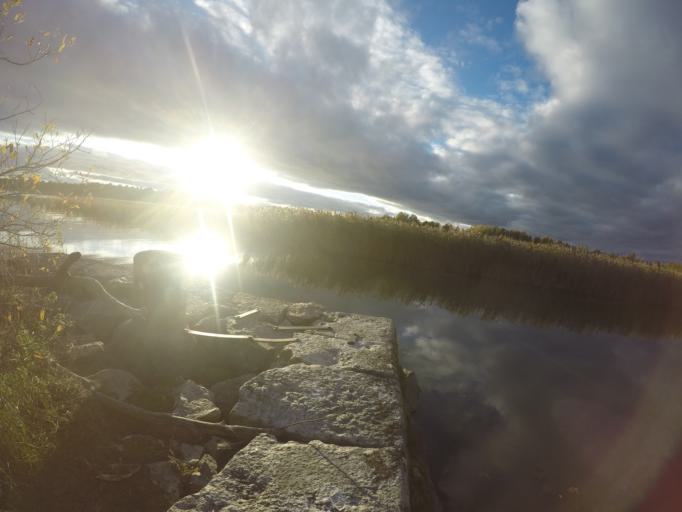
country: SE
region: Vaestmanland
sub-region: Arboga Kommun
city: Tyringe
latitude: 59.2910
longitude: 16.0028
